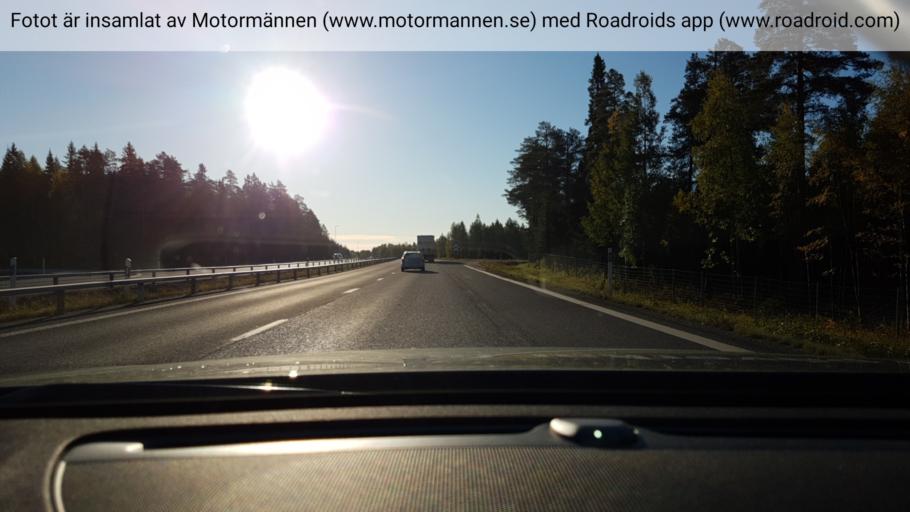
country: SE
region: Norrbotten
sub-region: Lulea Kommun
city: Gammelstad
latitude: 65.6261
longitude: 22.0521
